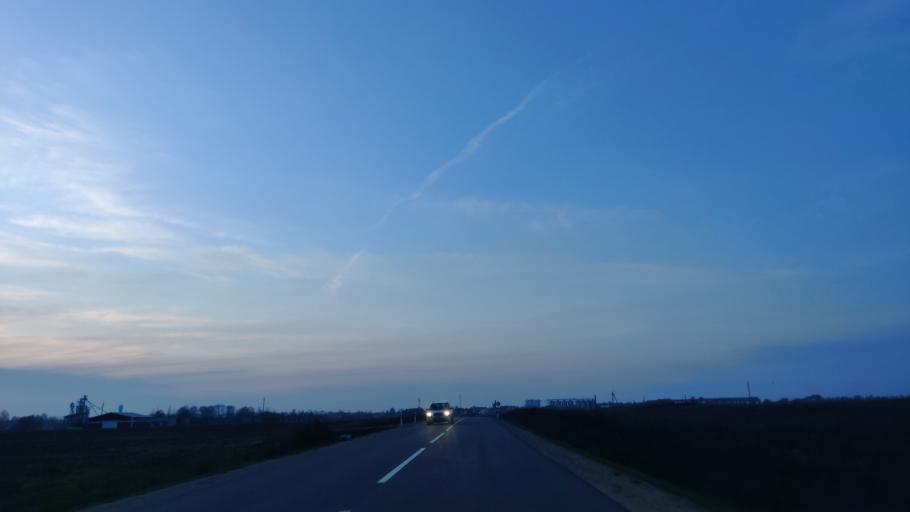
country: LT
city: Lentvaris
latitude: 54.6059
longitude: 24.9984
